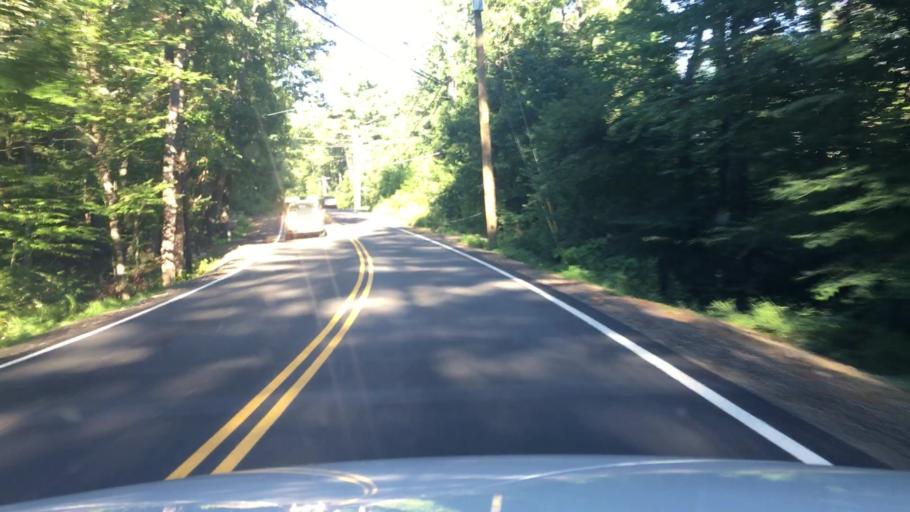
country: US
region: New Hampshire
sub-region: Rockingham County
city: Sandown
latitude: 42.9120
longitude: -71.1766
